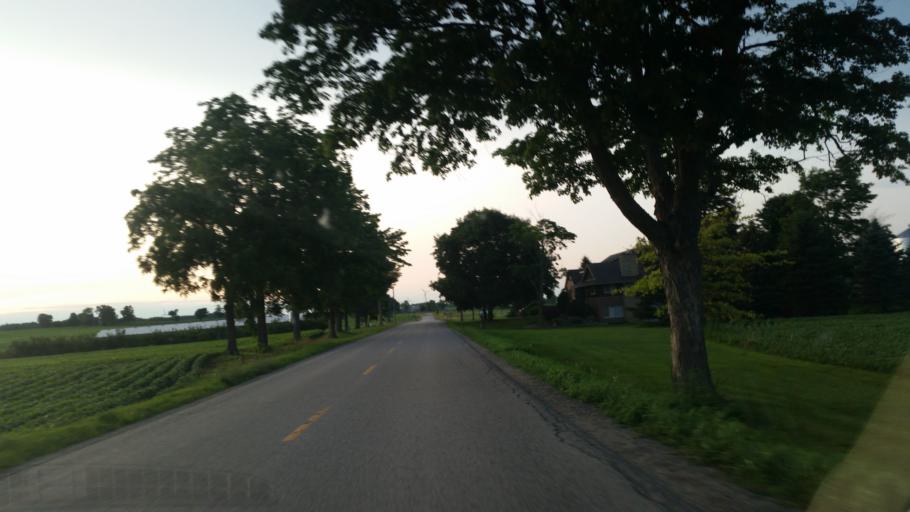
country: CA
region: Ontario
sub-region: Oxford County
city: Woodstock
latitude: 43.0318
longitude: -80.6556
